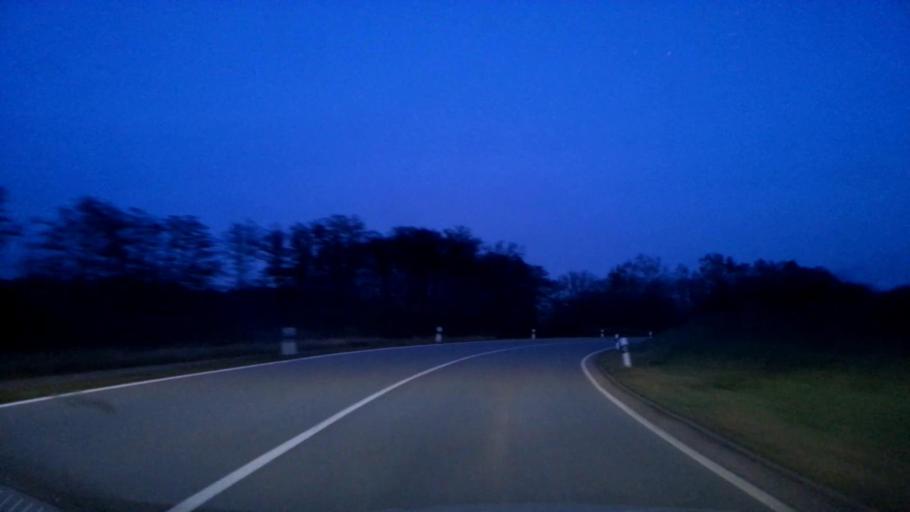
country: DE
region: Bavaria
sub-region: Upper Franconia
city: Pettstadt
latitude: 49.8420
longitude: 10.9212
